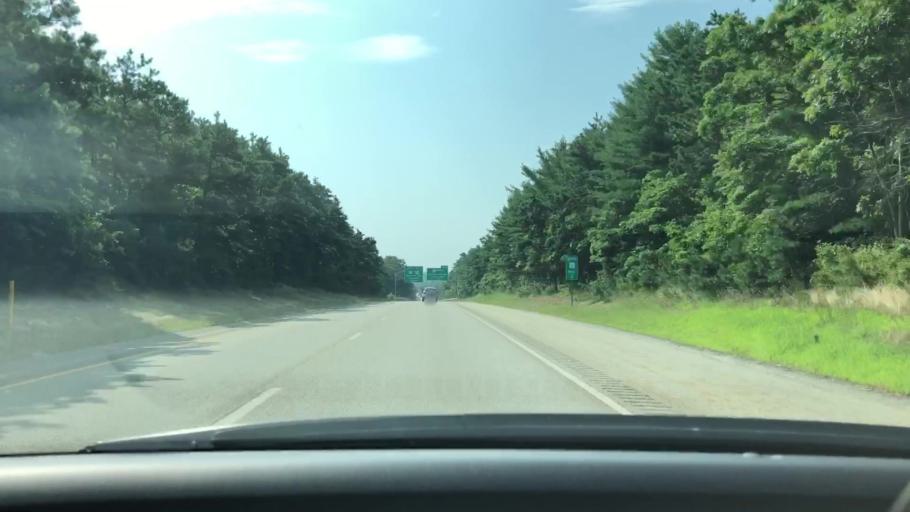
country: US
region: Massachusetts
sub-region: Barnstable County
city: Sagamore
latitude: 41.8212
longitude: -70.5576
